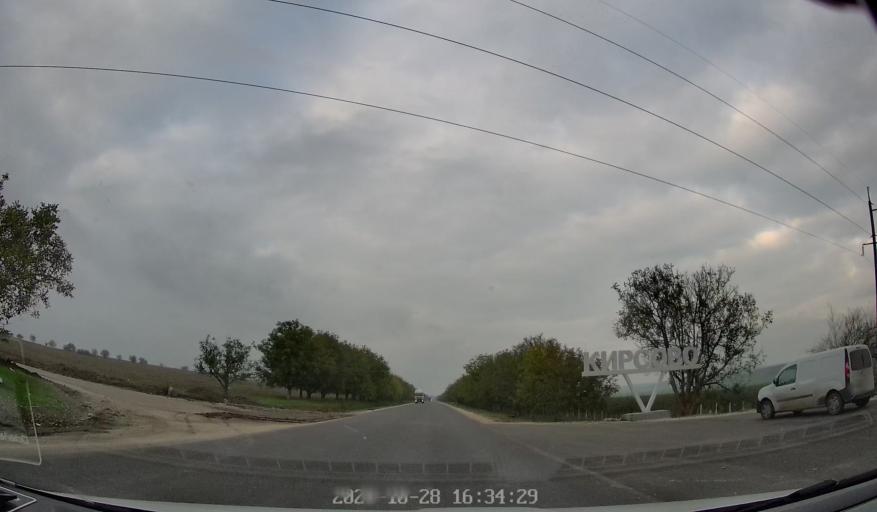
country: MD
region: Gagauzia
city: Comrat
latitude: 46.1934
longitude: 28.6332
